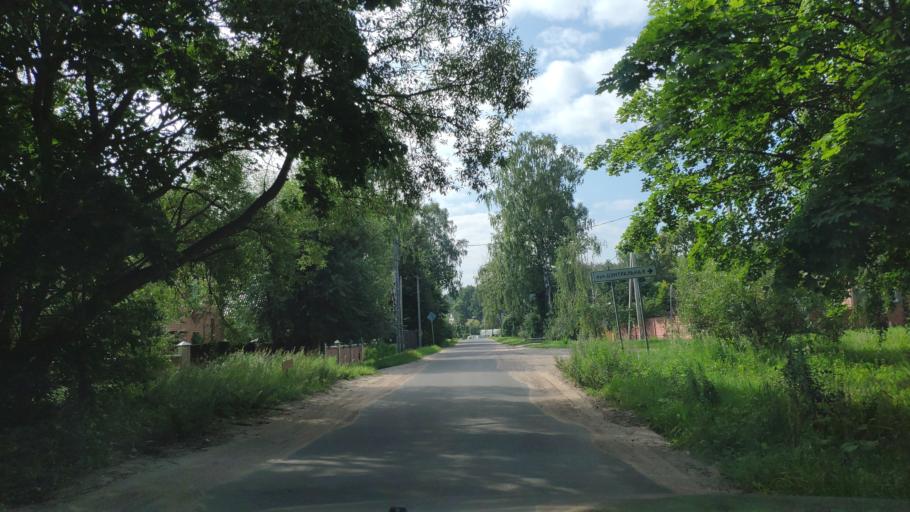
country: BY
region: Minsk
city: Zaslawye
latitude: 53.9921
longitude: 27.2845
